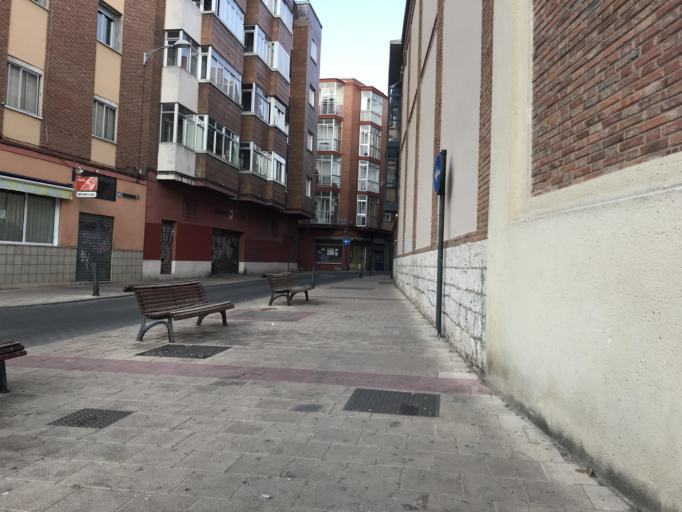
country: ES
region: Castille and Leon
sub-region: Provincia de Valladolid
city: Valladolid
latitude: 41.6558
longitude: -4.7208
